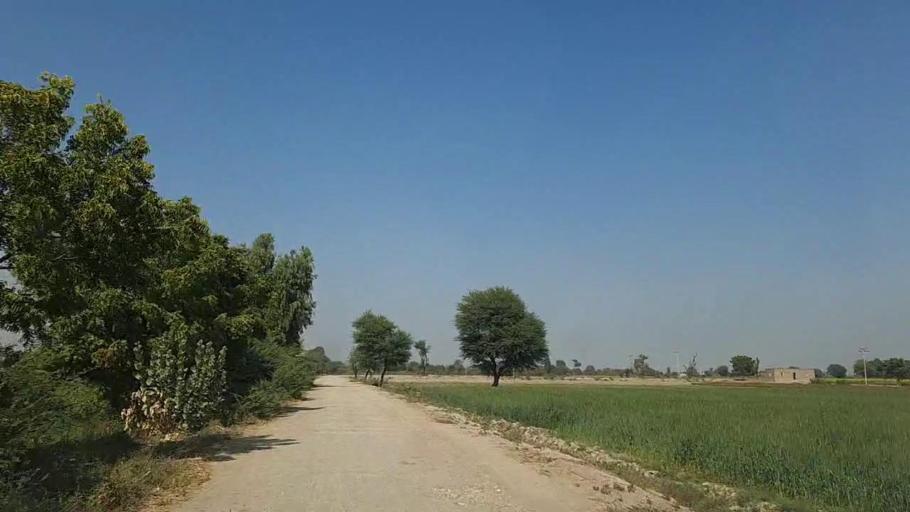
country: PK
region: Sindh
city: Naukot
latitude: 24.8552
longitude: 69.4156
